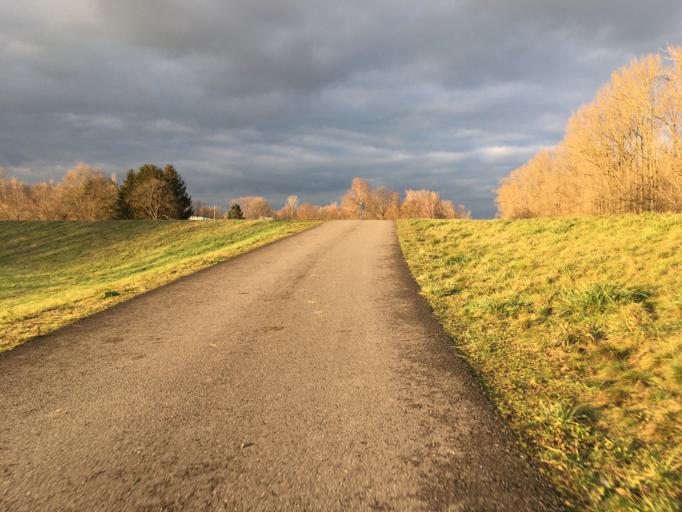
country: DE
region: Rheinland-Pfalz
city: Speyer
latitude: 49.2773
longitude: 8.4222
